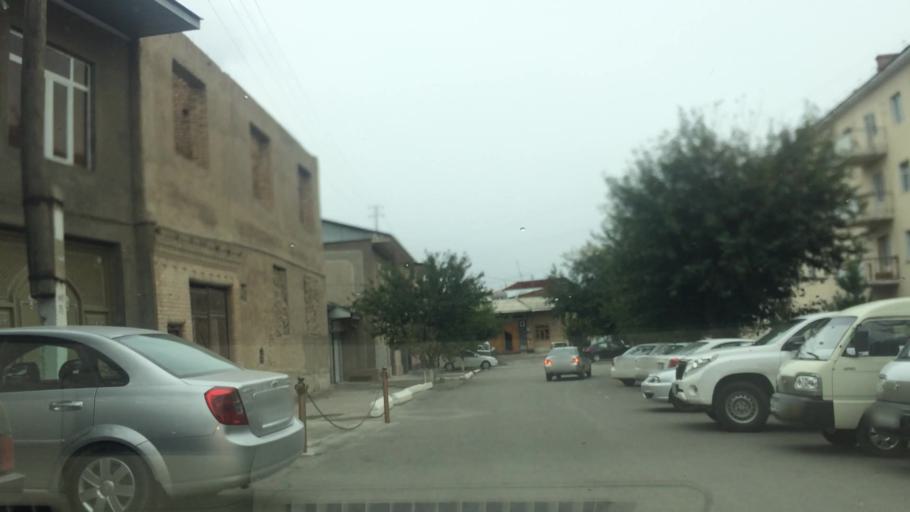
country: UZ
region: Samarqand
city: Samarqand
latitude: 39.6530
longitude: 66.9760
